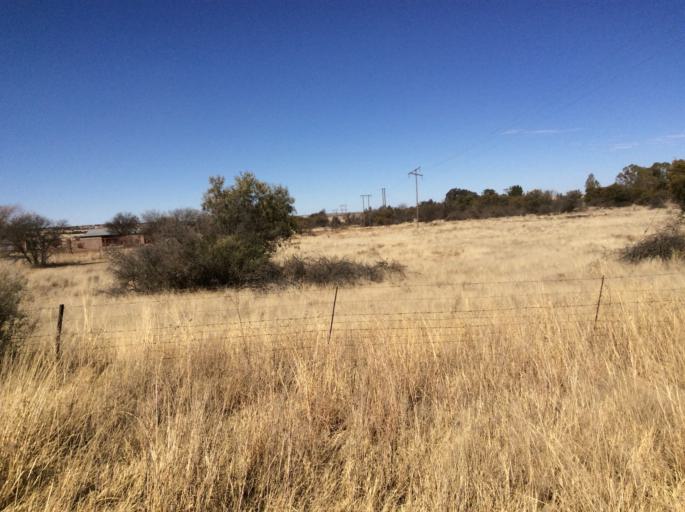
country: ZA
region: Orange Free State
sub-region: Lejweleputswa District Municipality
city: Brandfort
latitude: -28.7161
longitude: 26.0629
